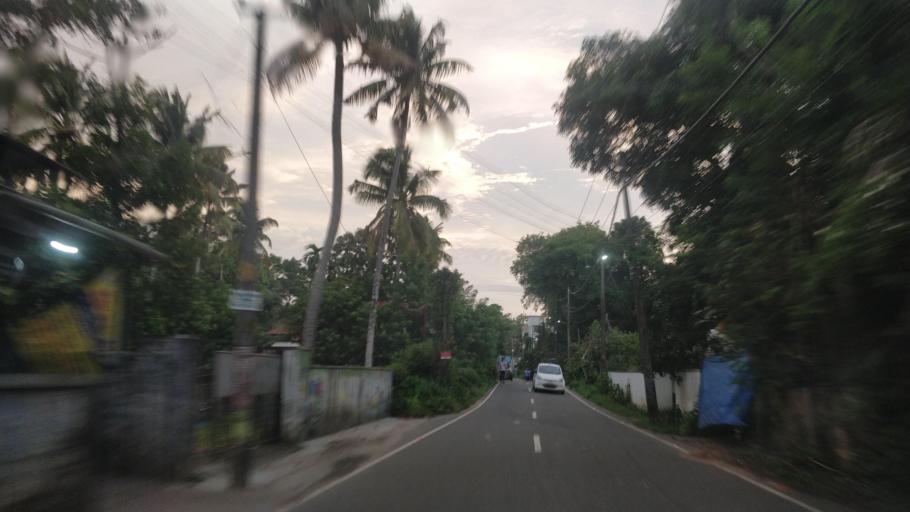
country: IN
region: Kerala
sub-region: Thrissur District
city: Kodungallur
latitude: 10.1418
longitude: 76.1891
